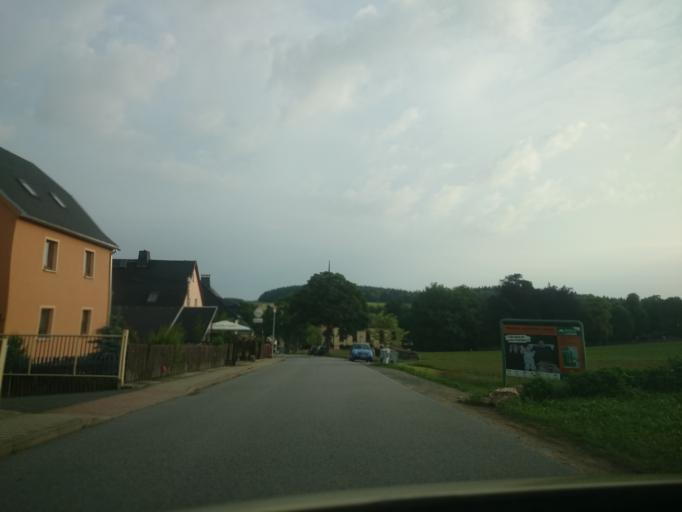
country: DE
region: Saxony
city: Bornichen
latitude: 50.7475
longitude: 13.1434
